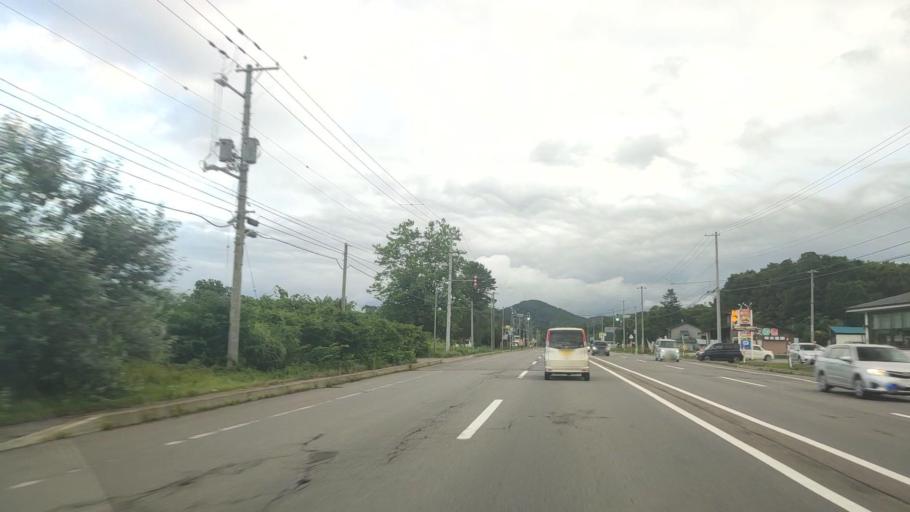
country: JP
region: Hokkaido
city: Nanae
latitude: 42.0047
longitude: 140.6329
